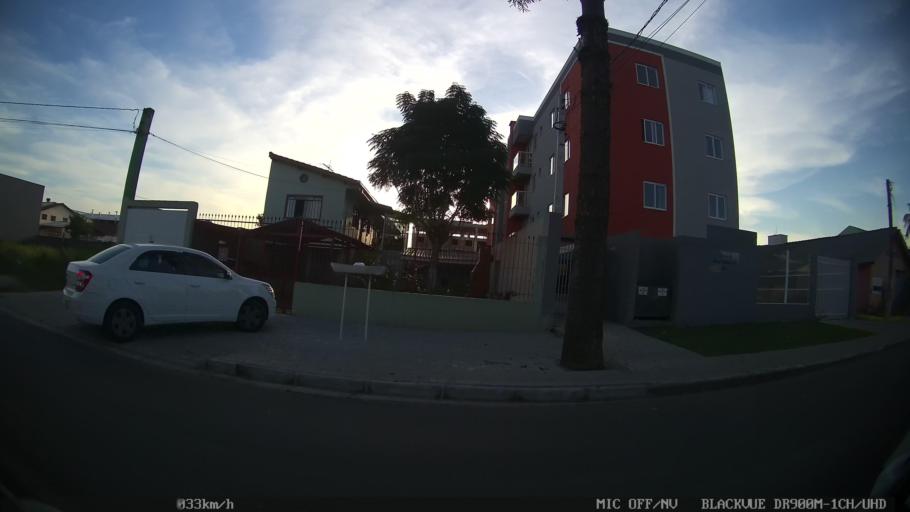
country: BR
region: Parana
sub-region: Pinhais
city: Pinhais
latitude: -25.4513
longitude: -49.1761
